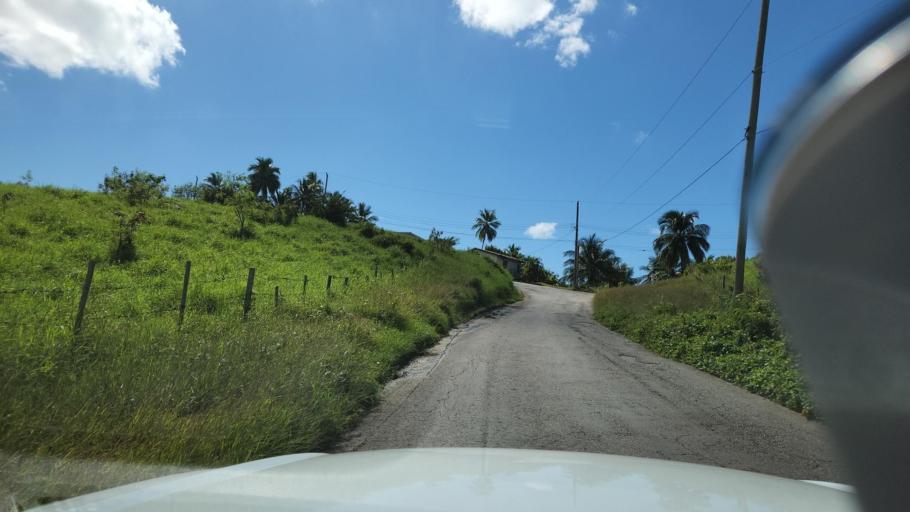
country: BB
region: Saint Thomas
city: Welchman Hall
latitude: 13.2115
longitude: -59.5590
